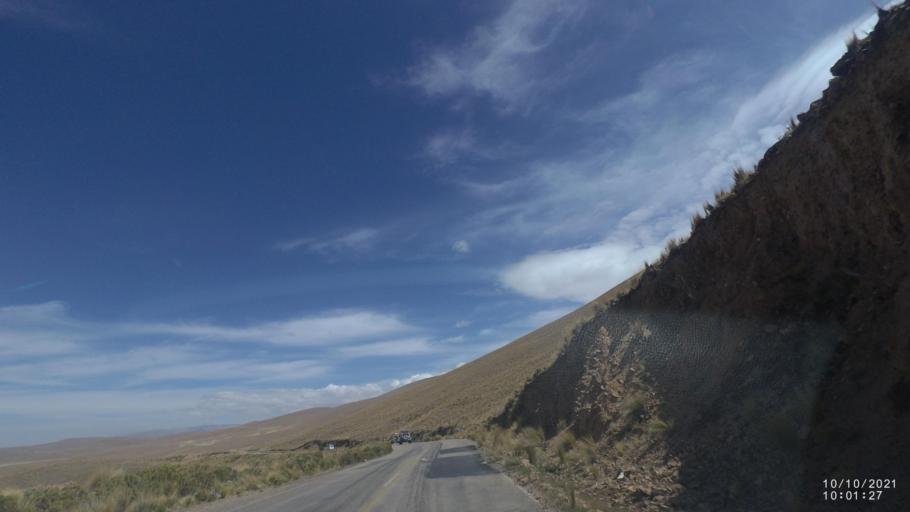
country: BO
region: La Paz
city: Eucaliptus
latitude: -17.3657
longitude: -67.4223
